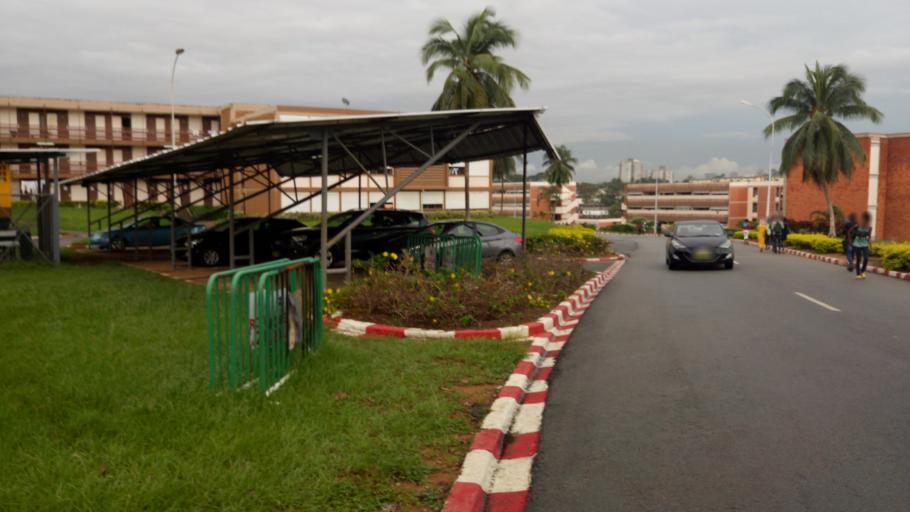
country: CI
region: Lagunes
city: Abidjan
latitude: 5.3413
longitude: -3.9889
